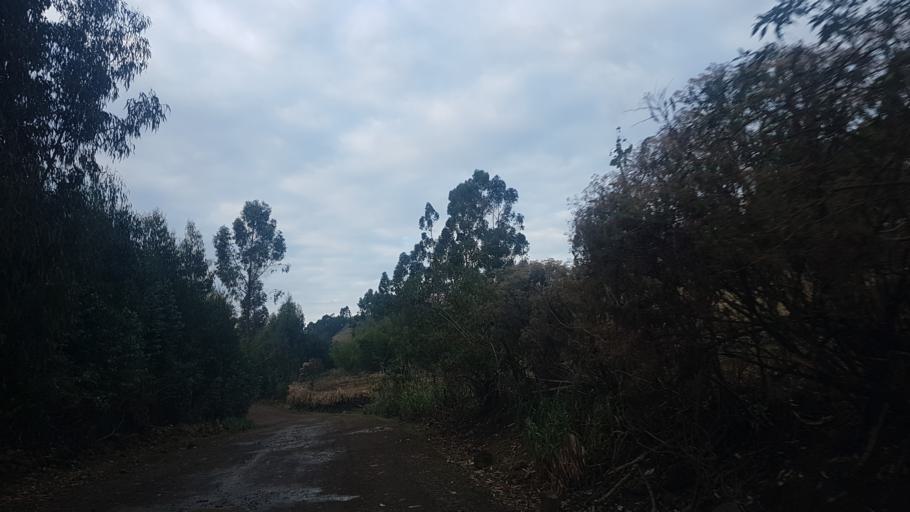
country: ET
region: Amhara
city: Finote Selam
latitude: 10.8027
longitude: 37.6625
